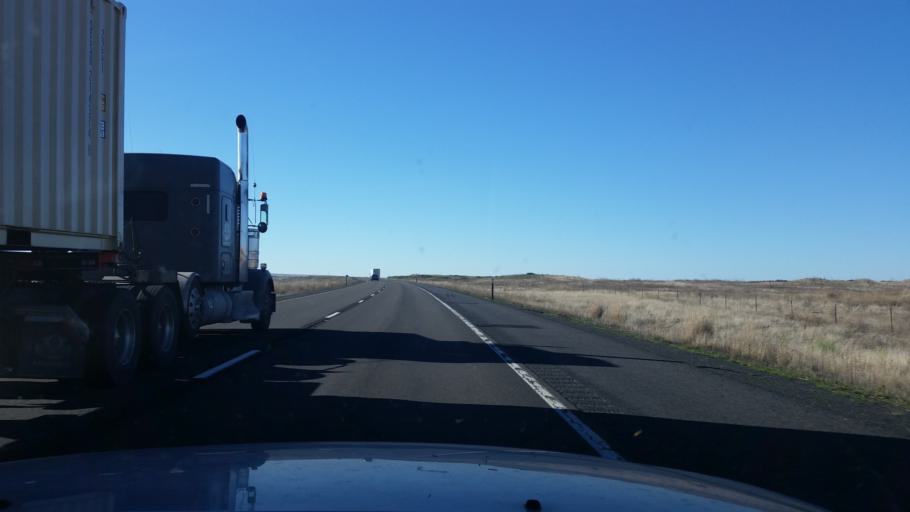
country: US
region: Washington
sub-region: Adams County
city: Ritzville
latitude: 47.2524
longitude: -118.1018
